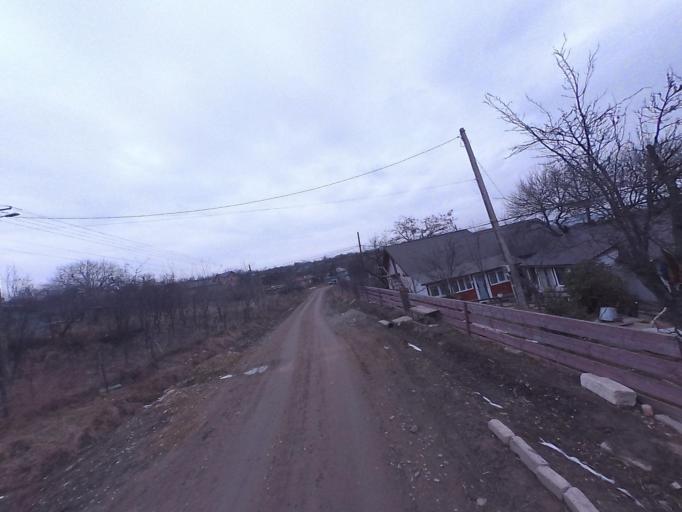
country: RO
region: Iasi
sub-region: Comuna Popricani
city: Popricani
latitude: 47.2944
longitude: 27.5083
